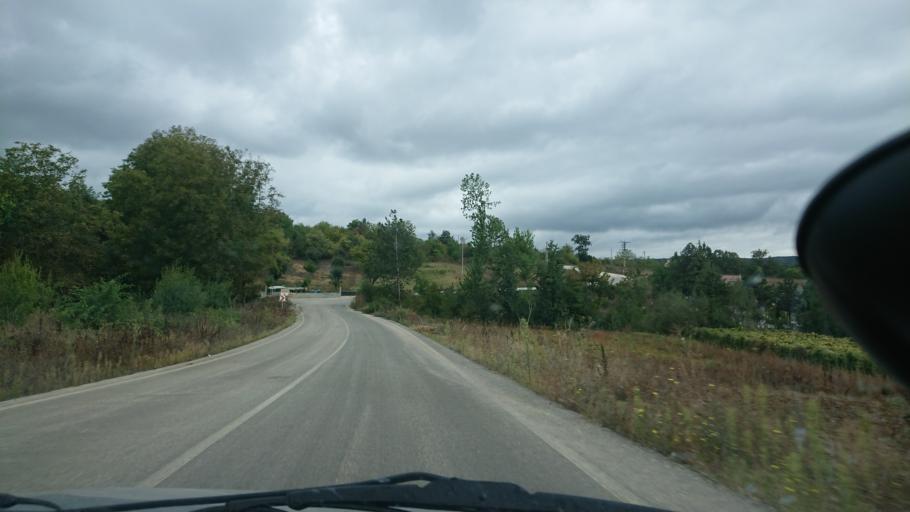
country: TR
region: Bilecik
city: Pazaryeri
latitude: 40.0105
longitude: 29.8034
